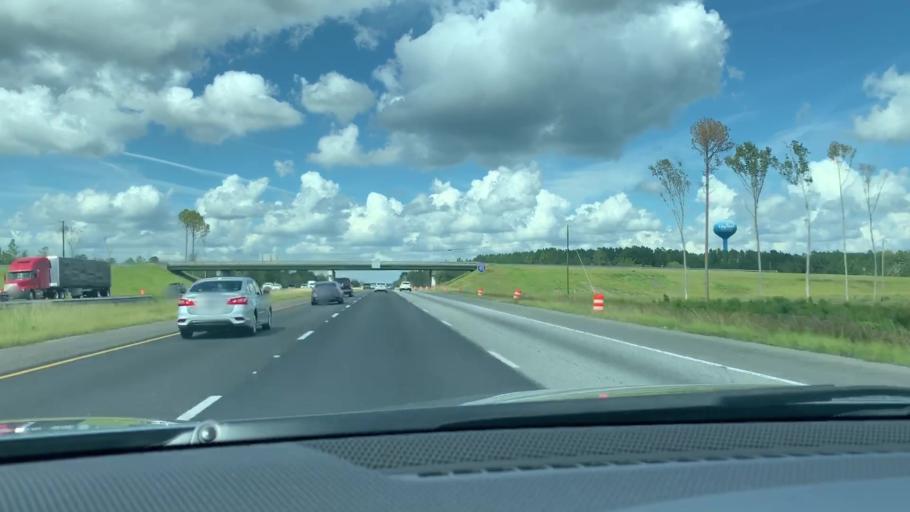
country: US
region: Georgia
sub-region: Camden County
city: Kingsland
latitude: 30.8450
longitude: -81.6713
